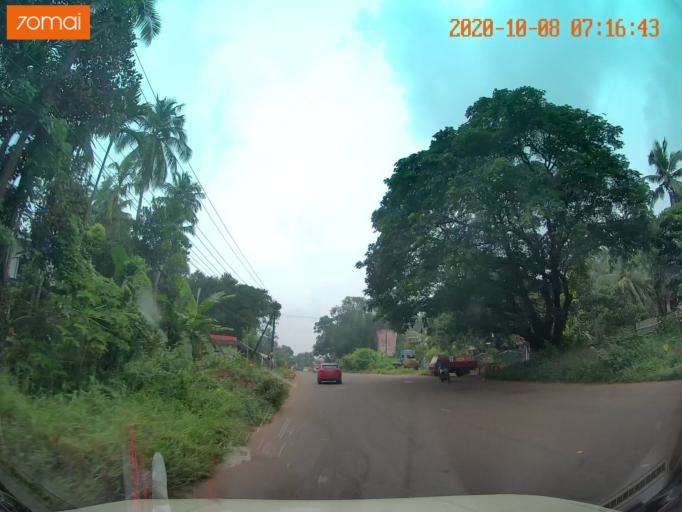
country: IN
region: Kerala
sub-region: Malappuram
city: Ponnani
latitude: 10.8329
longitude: 76.0187
